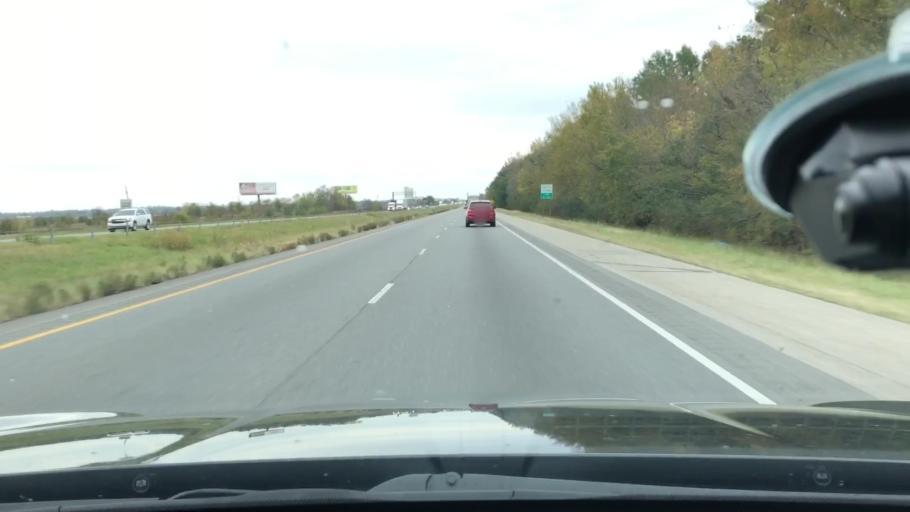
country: US
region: Arkansas
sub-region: Miller County
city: Texarkana
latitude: 33.4905
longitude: -93.9700
